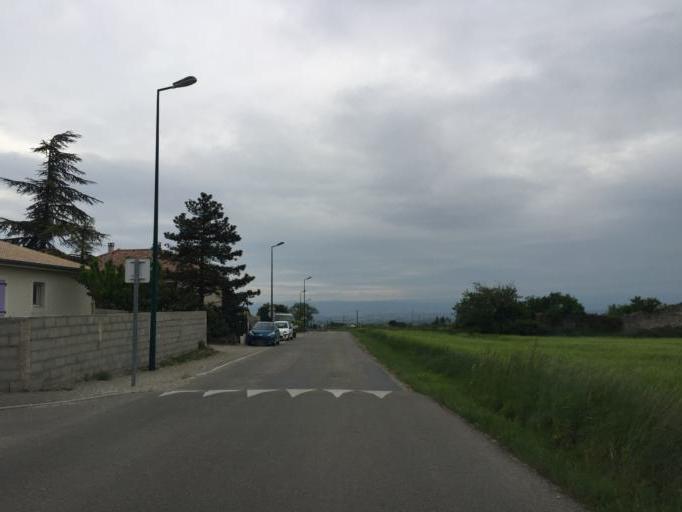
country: FR
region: Rhone-Alpes
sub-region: Departement de la Drome
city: Chatuzange-le-Goubet
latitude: 44.9564
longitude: 5.1329
